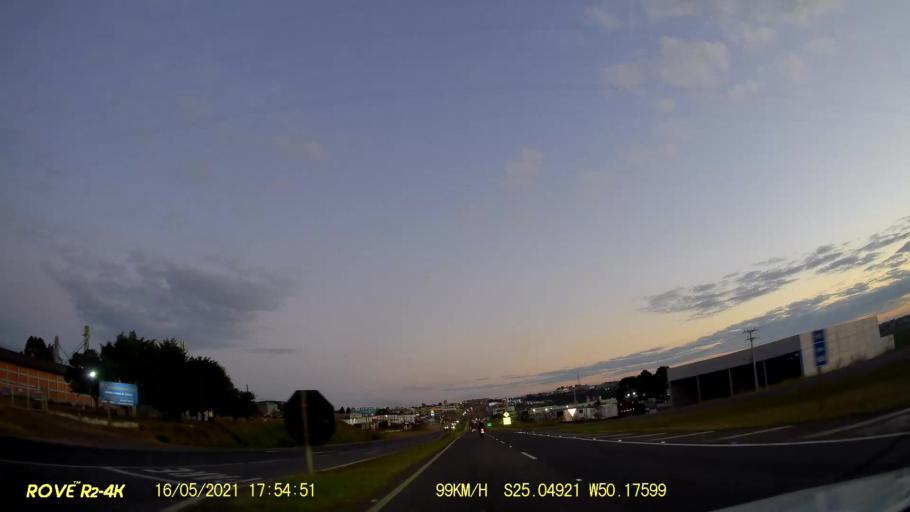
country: BR
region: Parana
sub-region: Ponta Grossa
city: Ponta Grossa
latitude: -25.0493
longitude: -50.1760
